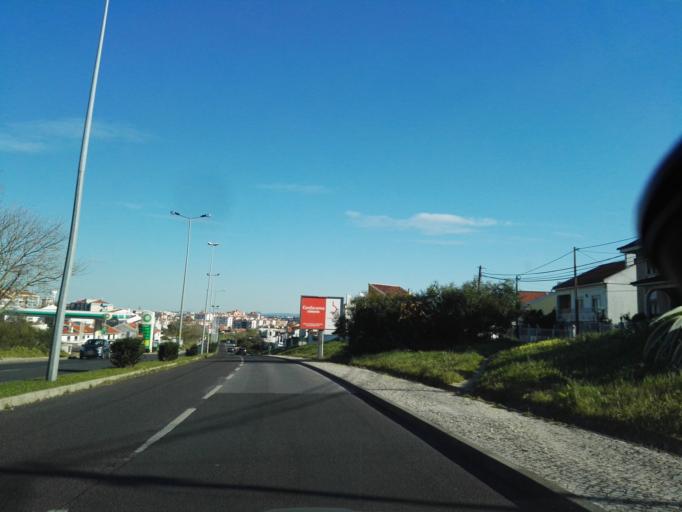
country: PT
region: Setubal
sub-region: Seixal
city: Corroios
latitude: 38.6486
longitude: -9.1643
